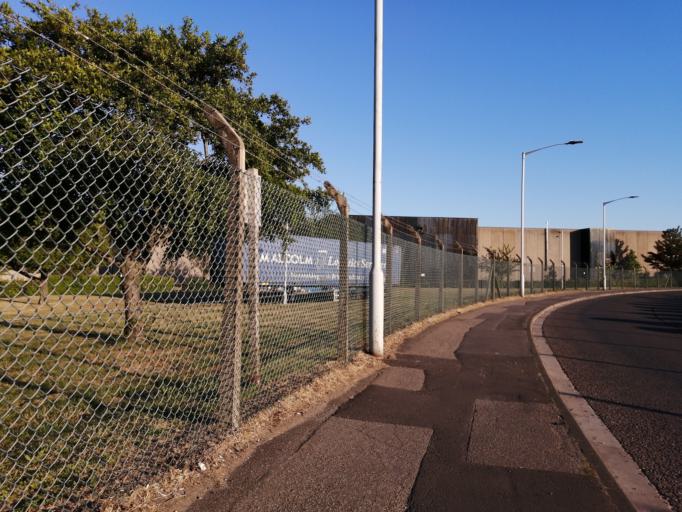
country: GB
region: England
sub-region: Peterborough
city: Peterborough
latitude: 52.5922
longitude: -0.2647
